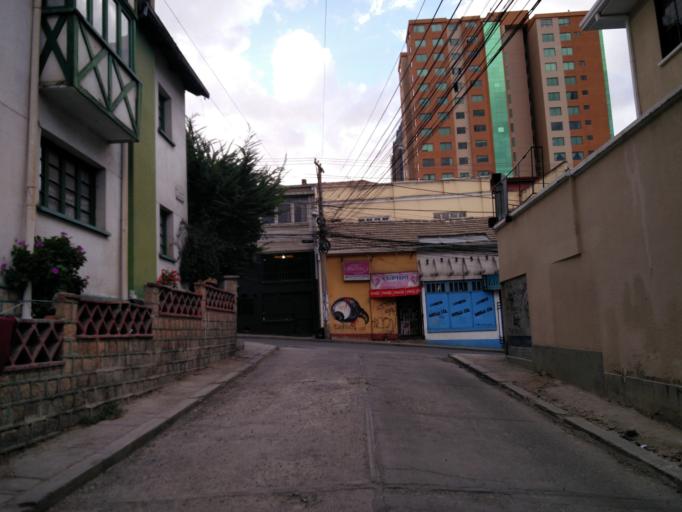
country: BO
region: La Paz
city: La Paz
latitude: -16.5112
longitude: -68.1278
